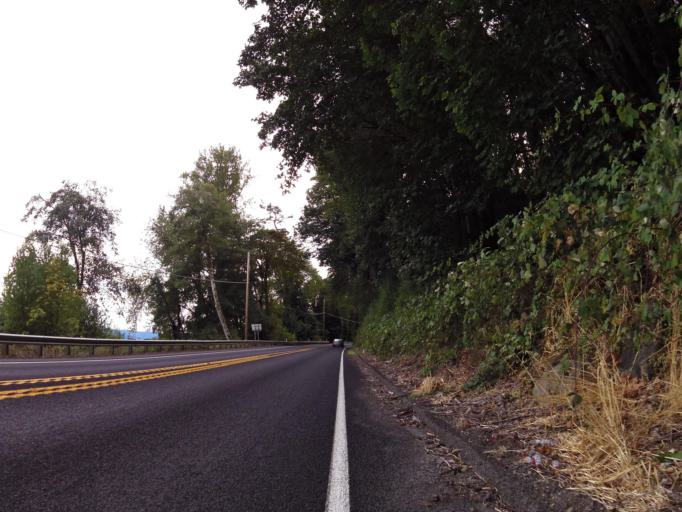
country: US
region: Oregon
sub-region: Columbia County
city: Clatskanie
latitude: 46.1740
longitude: -123.2204
